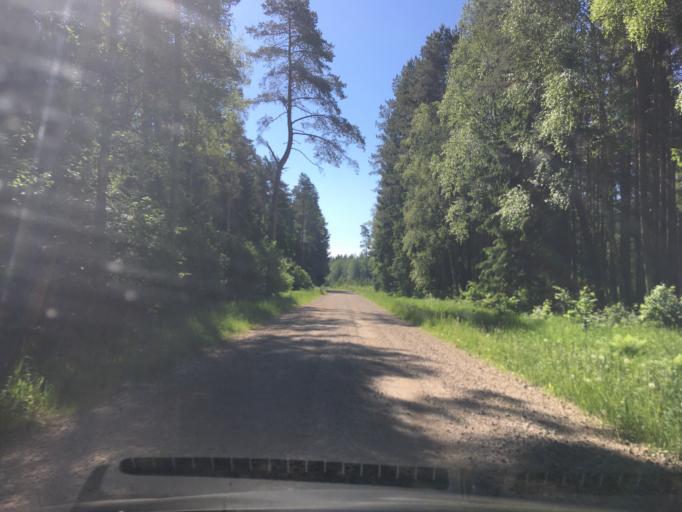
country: EE
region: Laeaene
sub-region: Lihula vald
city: Lihula
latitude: 58.6346
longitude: 23.7990
